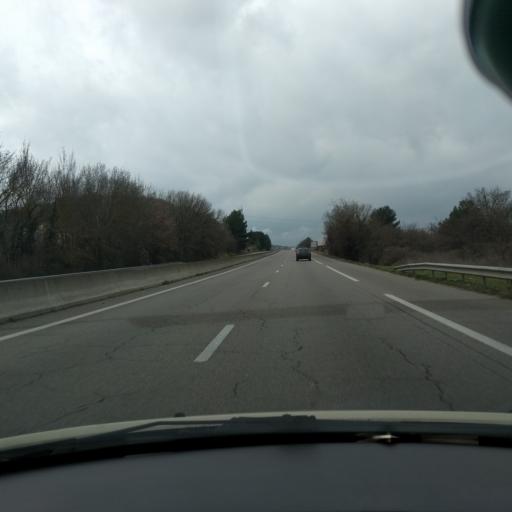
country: FR
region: Provence-Alpes-Cote d'Azur
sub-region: Departement des Bouches-du-Rhone
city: Simiane-Collongue
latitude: 43.4316
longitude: 5.4162
